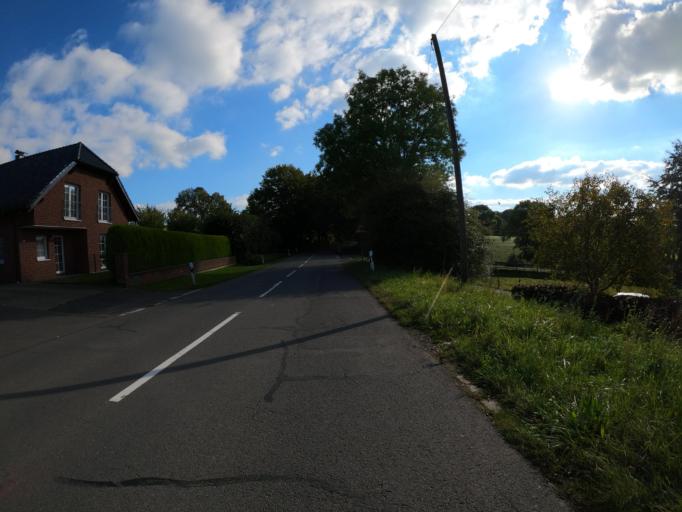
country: DE
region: North Rhine-Westphalia
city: Radevormwald
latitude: 51.2222
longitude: 7.3500
